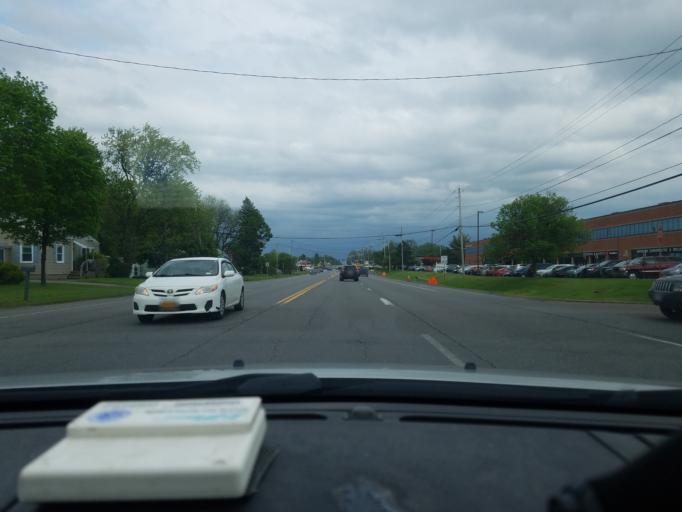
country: US
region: New York
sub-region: Onondaga County
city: Mattydale
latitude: 43.1219
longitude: -76.1635
